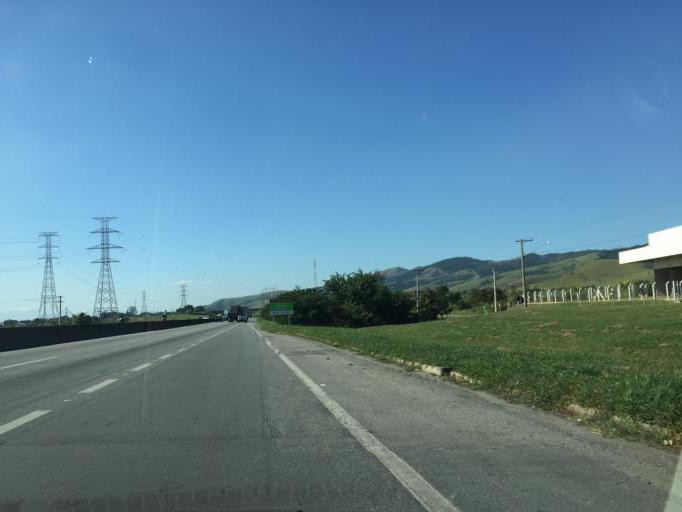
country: BR
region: Sao Paulo
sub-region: Aparecida
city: Aparecida
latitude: -22.9076
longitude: -45.3155
